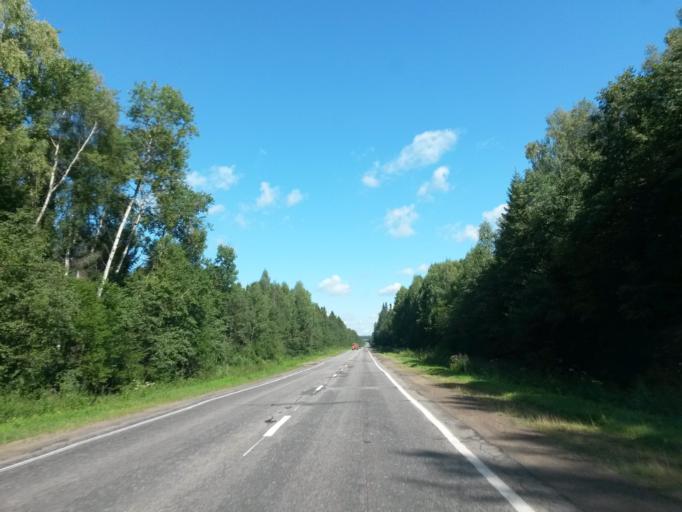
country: RU
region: Jaroslavl
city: Gavrilov-Yam
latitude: 57.4208
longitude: 39.9196
